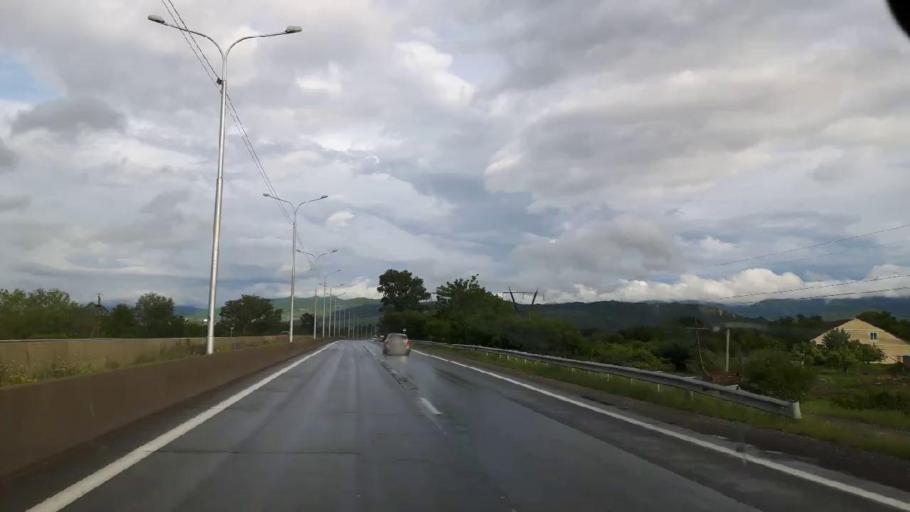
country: GE
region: Shida Kartli
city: Kaspi
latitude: 41.9191
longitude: 44.5503
